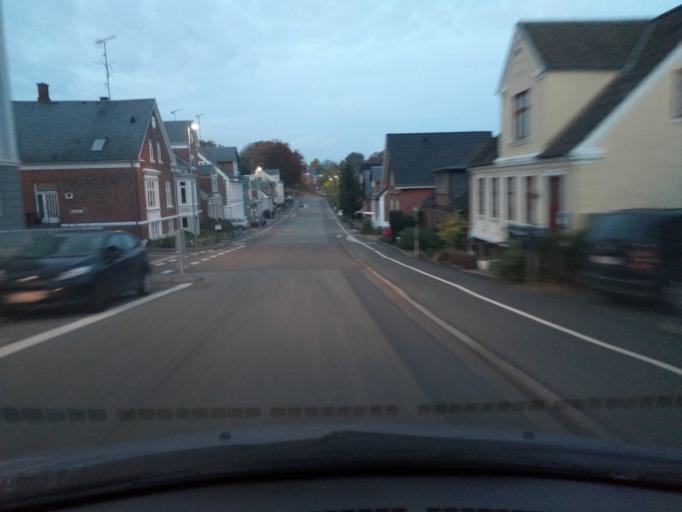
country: DK
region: South Denmark
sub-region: Svendborg Kommune
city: Svendborg
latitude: 55.0541
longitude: 10.5991
